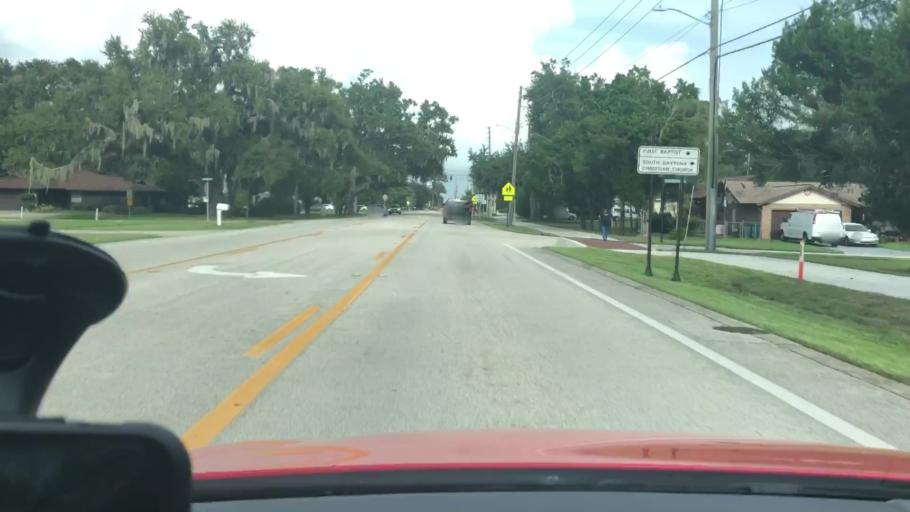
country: US
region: Florida
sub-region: Volusia County
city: South Daytona
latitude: 29.1708
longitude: -81.0121
